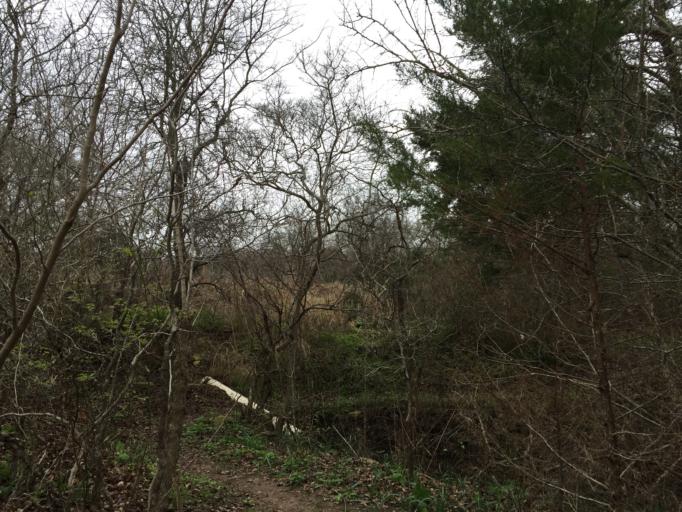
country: US
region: Texas
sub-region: Bastrop County
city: Bastrop
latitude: 30.0825
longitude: -97.3212
